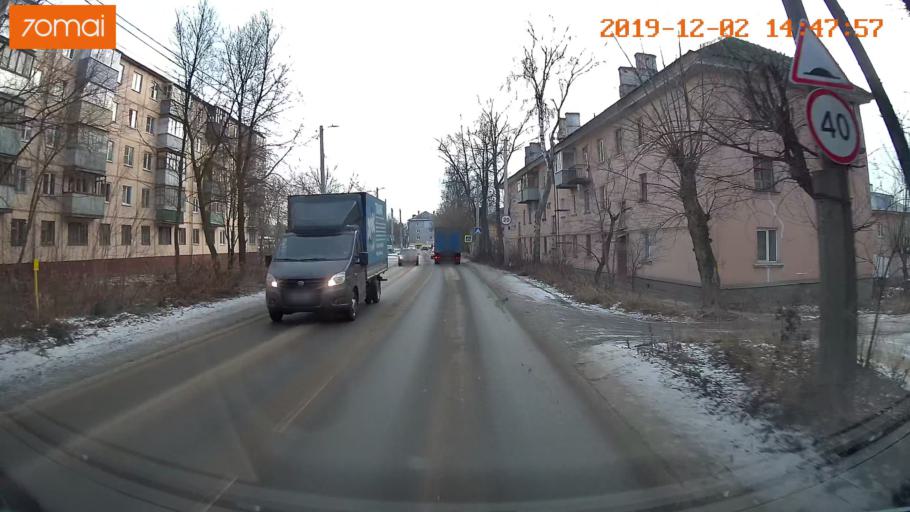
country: RU
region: Ivanovo
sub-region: Gorod Ivanovo
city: Ivanovo
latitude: 56.9861
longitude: 41.0175
